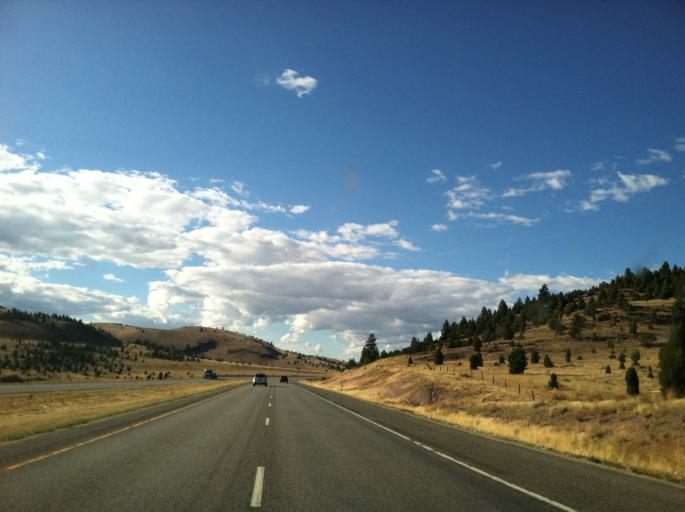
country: US
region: Montana
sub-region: Silver Bow County
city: Butte-Silver Bow (Balance)
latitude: 46.0223
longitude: -112.7253
